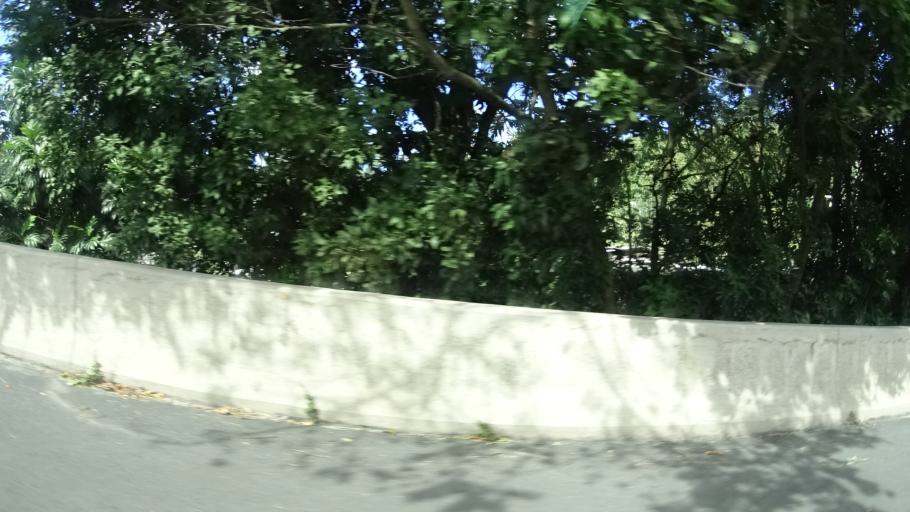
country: PR
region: Rio Grande
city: Palmer
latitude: 18.3710
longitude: -65.7745
